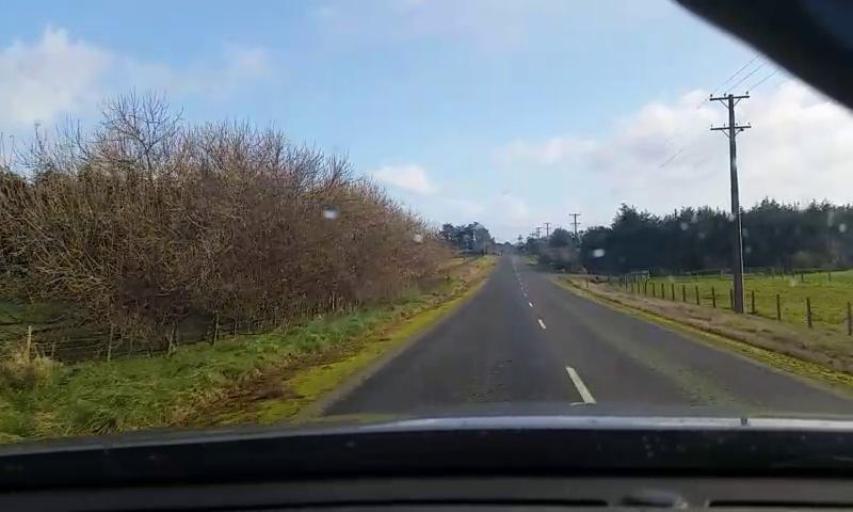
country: NZ
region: Southland
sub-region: Invercargill City
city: Invercargill
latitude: -46.3581
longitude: 168.3351
